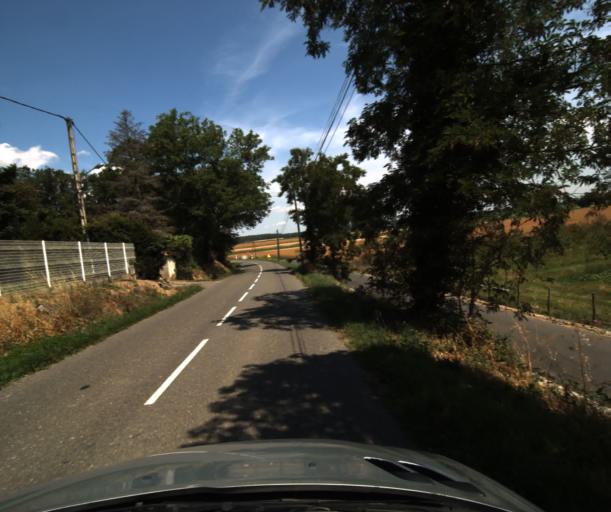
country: FR
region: Midi-Pyrenees
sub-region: Departement de la Haute-Garonne
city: Labastidette
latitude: 43.4726
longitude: 1.2175
